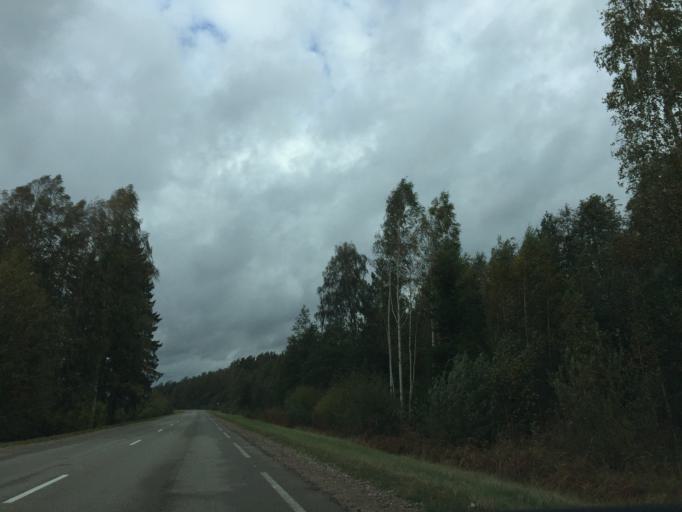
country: LV
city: Tireli
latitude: 56.8282
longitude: 23.6045
